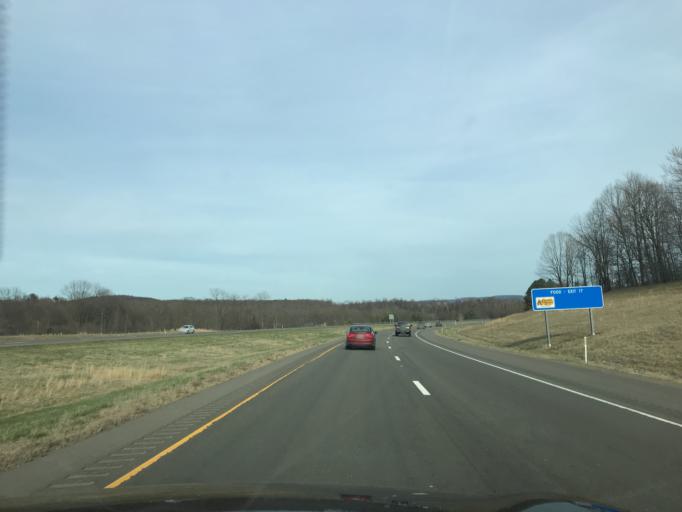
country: US
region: Pennsylvania
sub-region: Lycoming County
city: Montoursville
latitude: 41.2526
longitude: -76.8588
